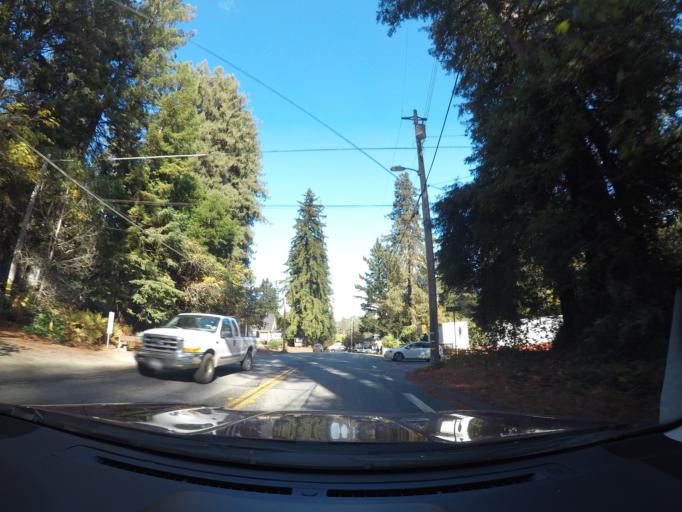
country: US
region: California
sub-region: Santa Cruz County
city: Boulder Creek
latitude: 37.1158
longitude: -122.1204
